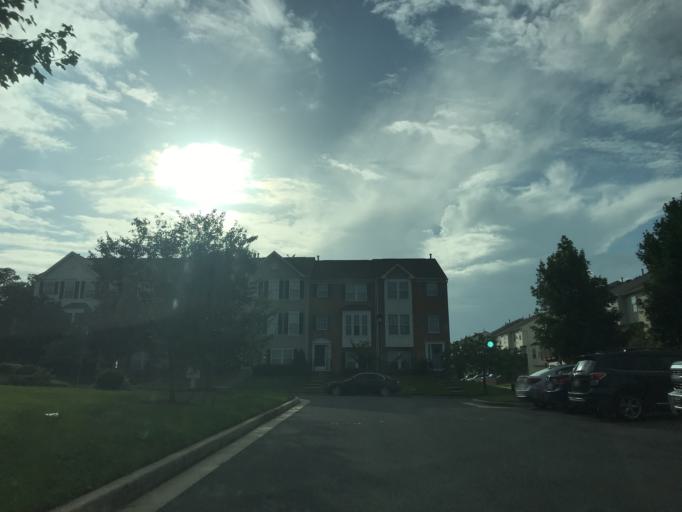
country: US
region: Maryland
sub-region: Baltimore County
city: Rossville
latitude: 39.3620
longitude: -76.4600
